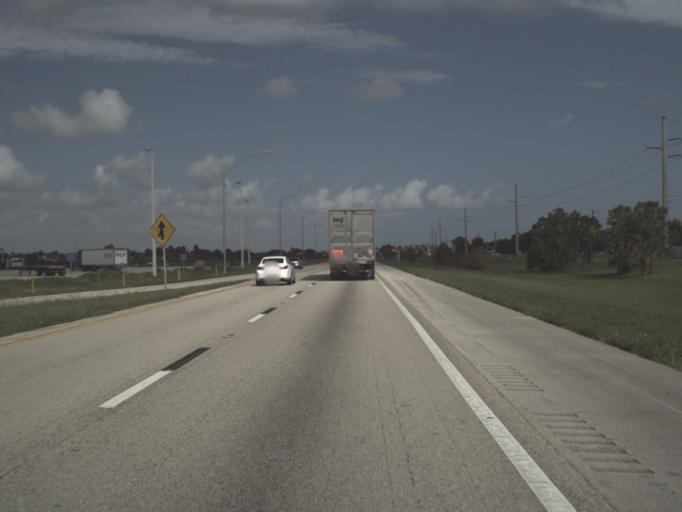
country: US
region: Florida
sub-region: Saint Lucie County
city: Port Saint Lucie
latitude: 27.3041
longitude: -80.3724
